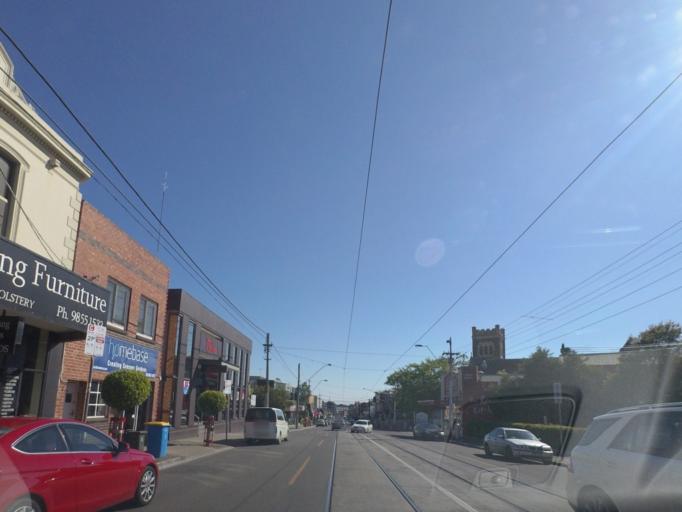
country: AU
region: Victoria
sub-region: Boroondara
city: Kew
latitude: -37.8053
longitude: 145.0350
